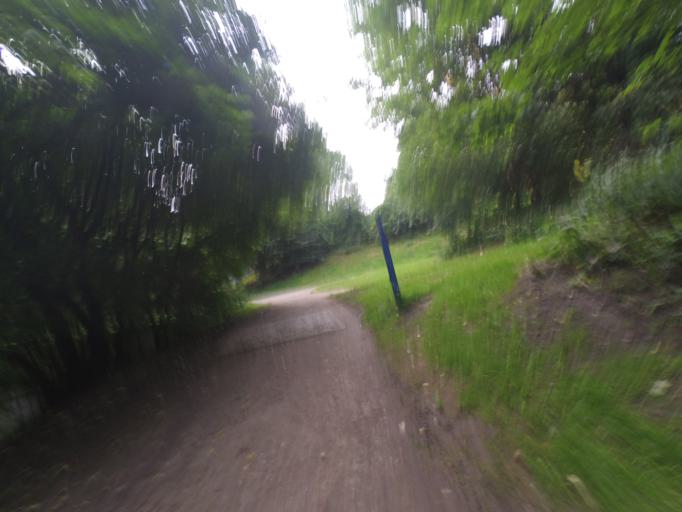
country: DE
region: Hamburg
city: Wandsbek
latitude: 53.5460
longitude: 10.1215
